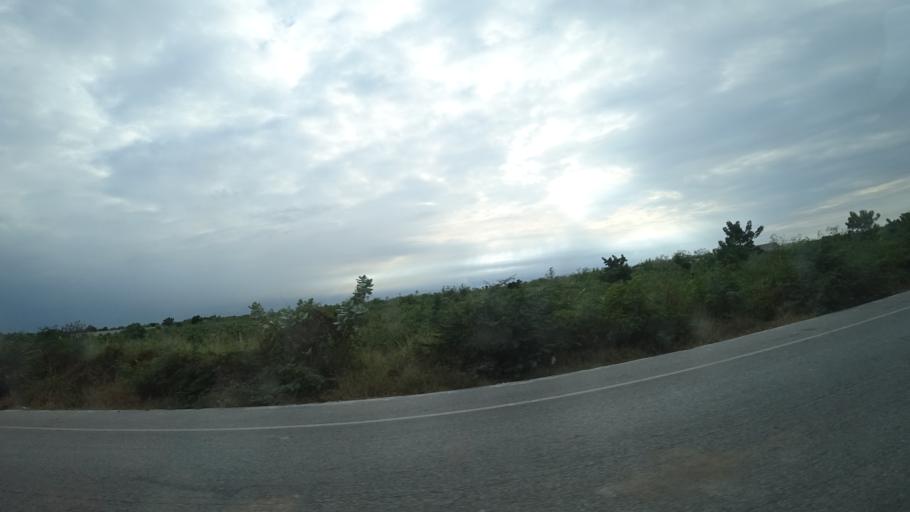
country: HT
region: Ouest
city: Croix des Bouquets
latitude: 18.6490
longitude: -72.2815
